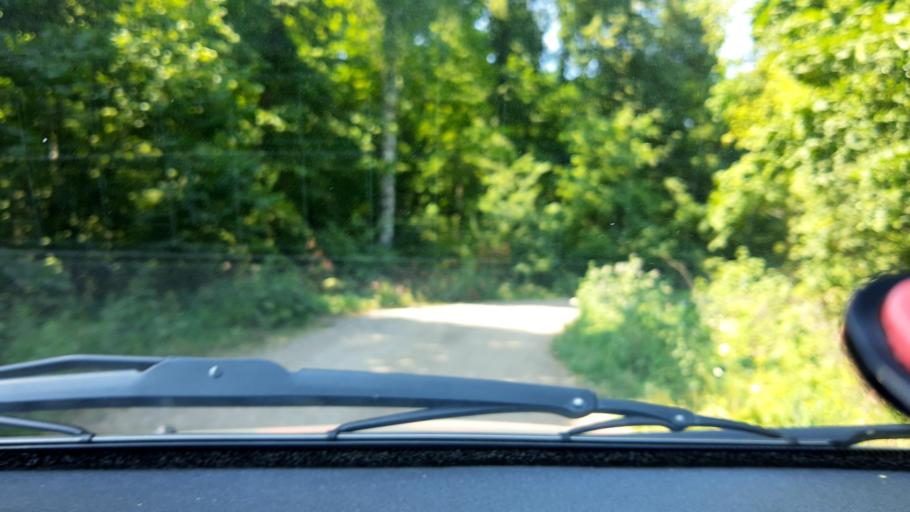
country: RU
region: Bashkortostan
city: Karmaskaly
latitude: 54.3822
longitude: 55.8969
